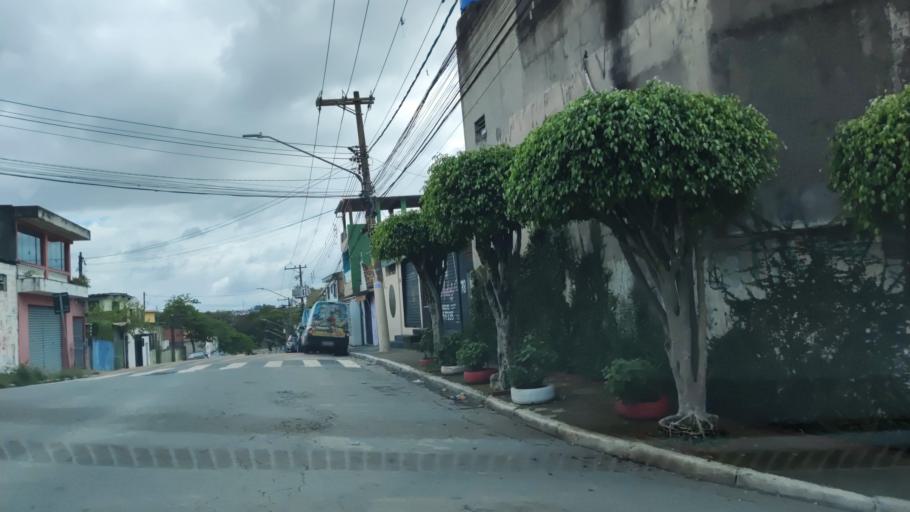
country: BR
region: Sao Paulo
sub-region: Sao Caetano Do Sul
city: Sao Caetano do Sul
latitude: -23.5966
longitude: -46.5004
